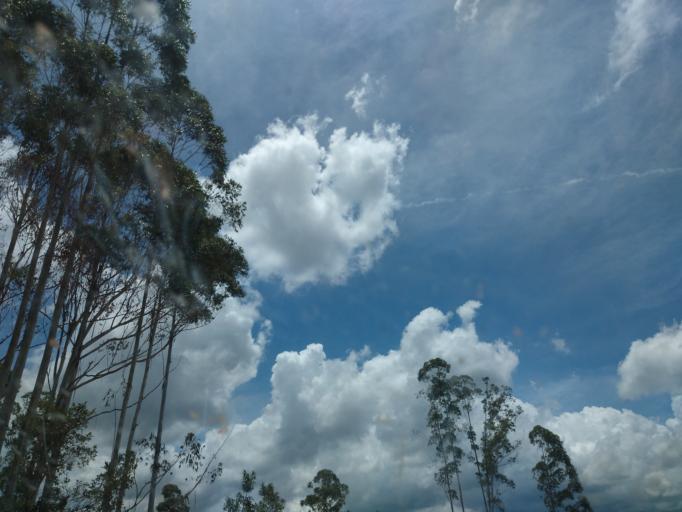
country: BR
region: Minas Gerais
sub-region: Sao Joao Del Rei
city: Sao Joao del Rei
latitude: -20.8945
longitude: -44.3056
